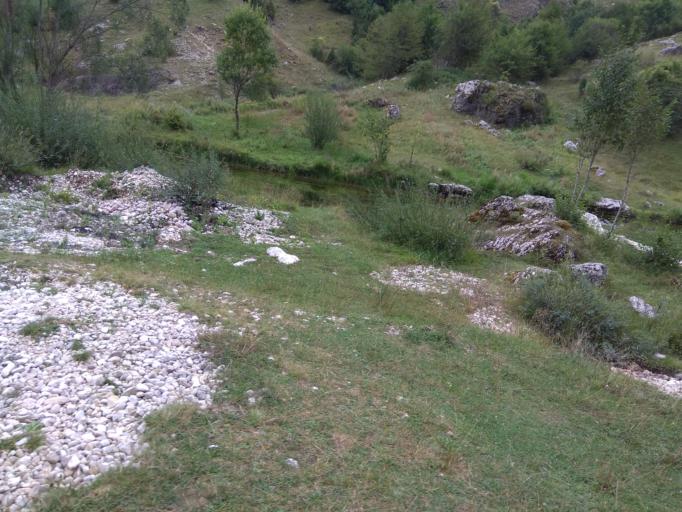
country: ME
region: Opstina Savnik
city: Savnik
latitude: 42.9885
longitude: 19.0678
